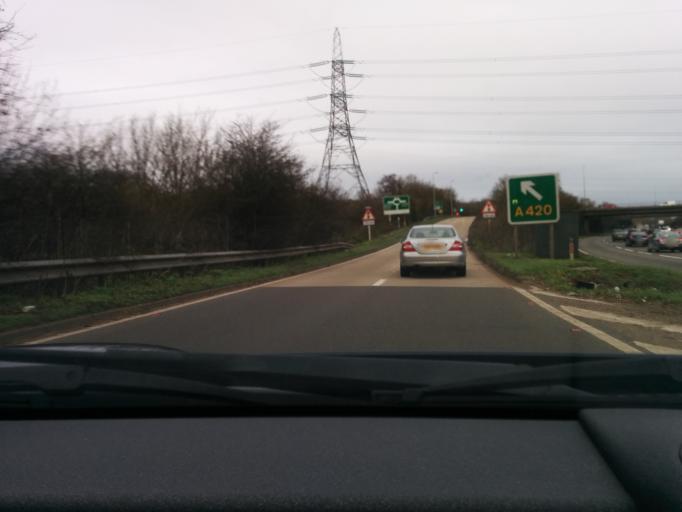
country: GB
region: England
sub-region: Oxfordshire
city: Boars Hill
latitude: 51.7539
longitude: -1.2970
